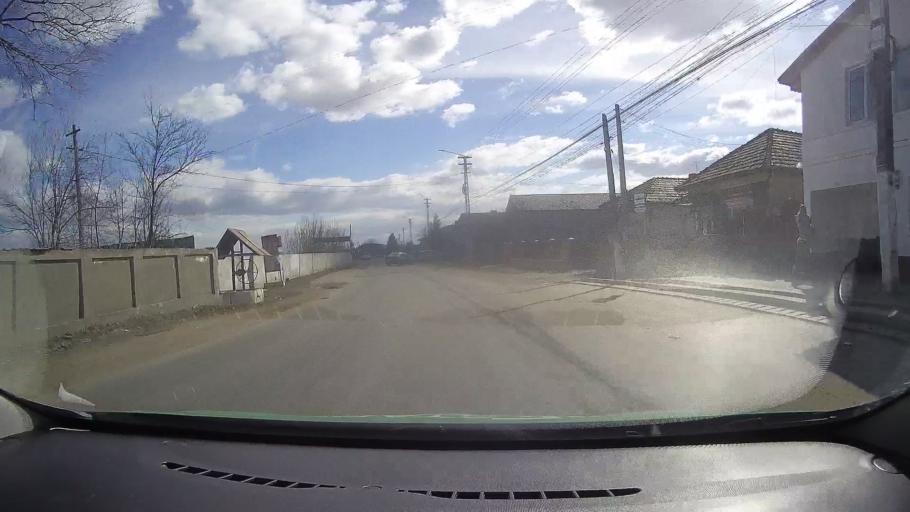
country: RO
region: Dambovita
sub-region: Comuna Doicesti
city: Doicesti
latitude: 44.9863
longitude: 25.3844
